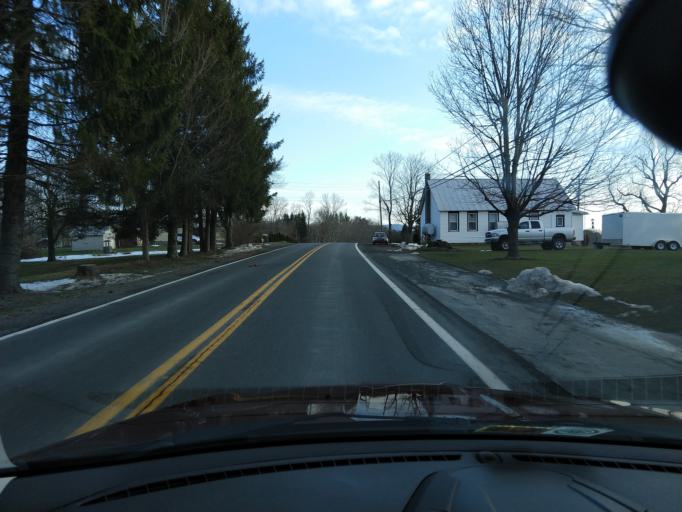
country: US
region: West Virginia
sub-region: Pocahontas County
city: Marlinton
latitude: 38.1048
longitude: -80.2748
